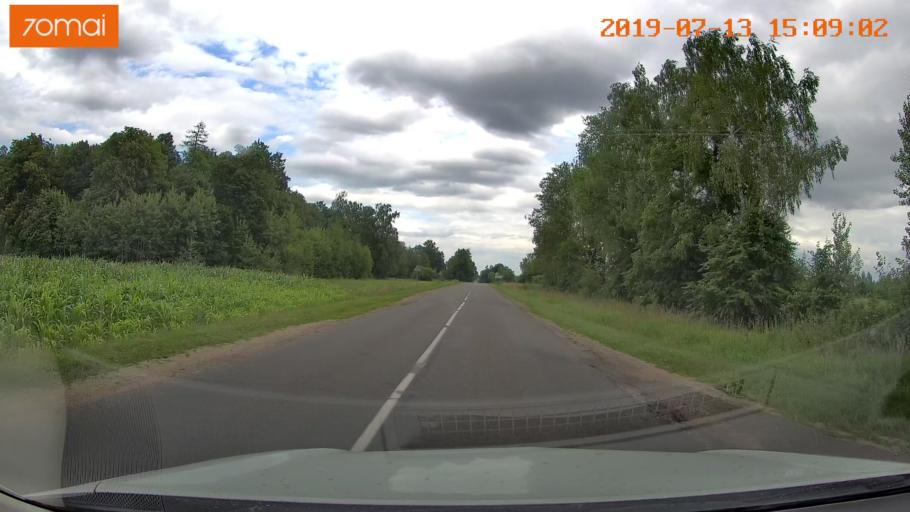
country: BY
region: Mogilev
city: Hlusha
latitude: 53.1744
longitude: 28.7558
